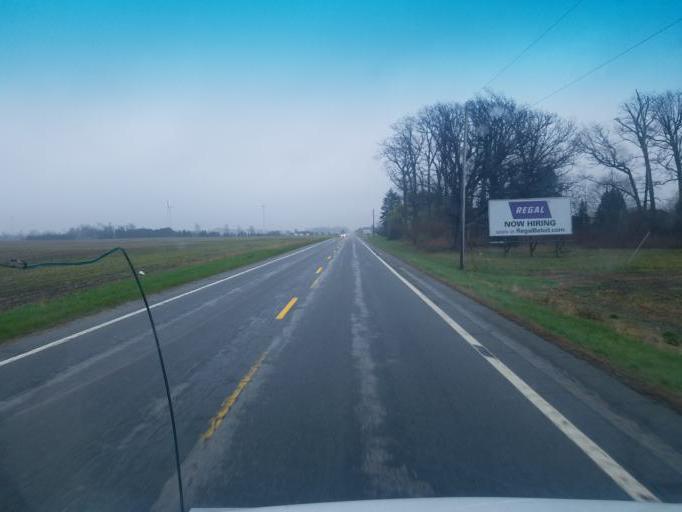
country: US
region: Ohio
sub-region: Wood County
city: Weston
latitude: 41.3722
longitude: -83.7576
